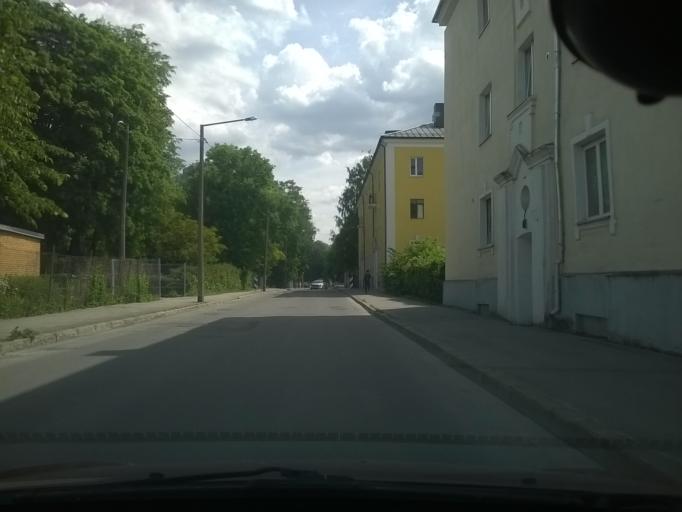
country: EE
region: Harju
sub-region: Tallinna linn
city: Tallinn
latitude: 59.4246
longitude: 24.7369
